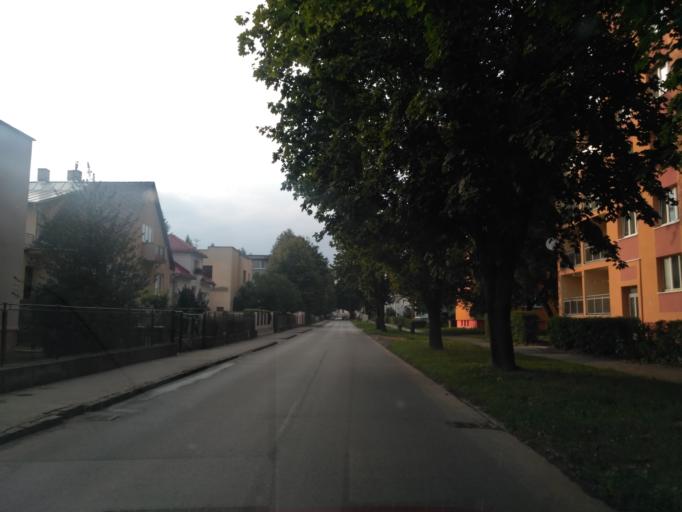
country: SK
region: Presovsky
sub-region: Okres Presov
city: Presov
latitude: 48.9981
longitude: 21.2215
